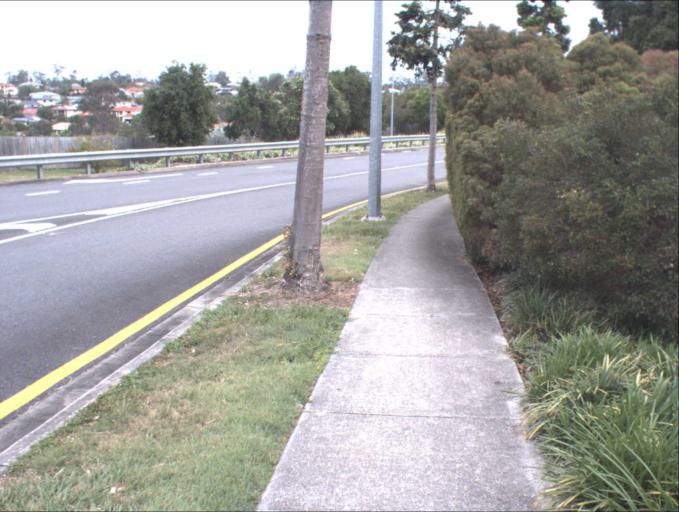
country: AU
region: Queensland
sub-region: Logan
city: Rochedale South
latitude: -27.6074
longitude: 153.1031
